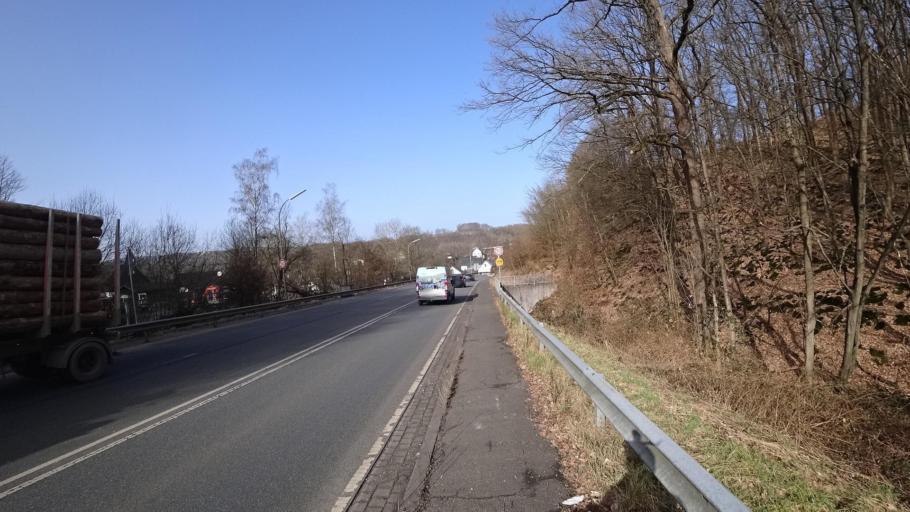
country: DE
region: Rheinland-Pfalz
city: Bruchertseifen
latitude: 50.7710
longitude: 7.7148
